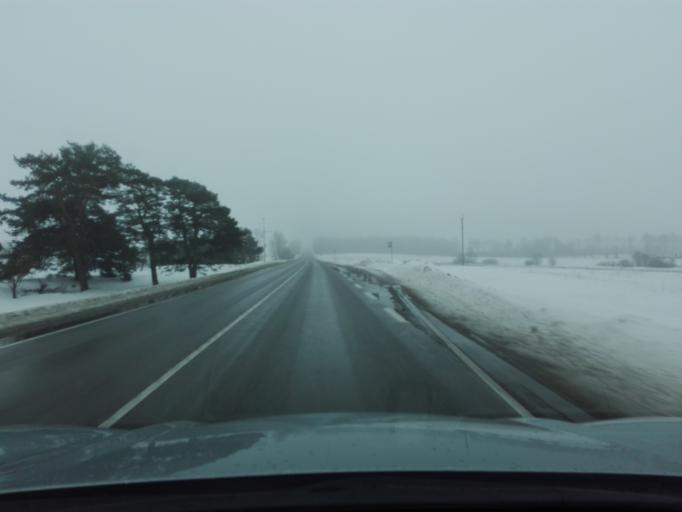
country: EE
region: Harju
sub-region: Saku vald
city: Saku
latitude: 59.2812
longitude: 24.7411
